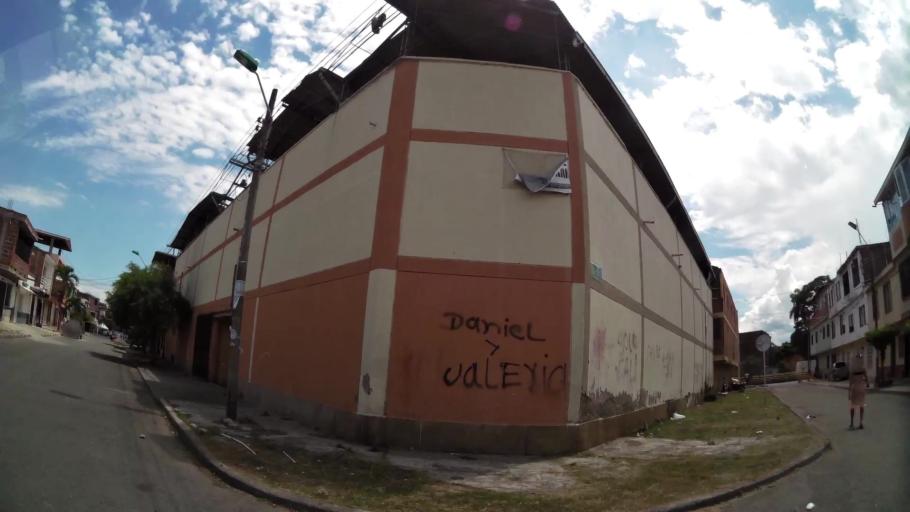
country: CO
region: Valle del Cauca
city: Cali
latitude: 3.4384
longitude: -76.5179
